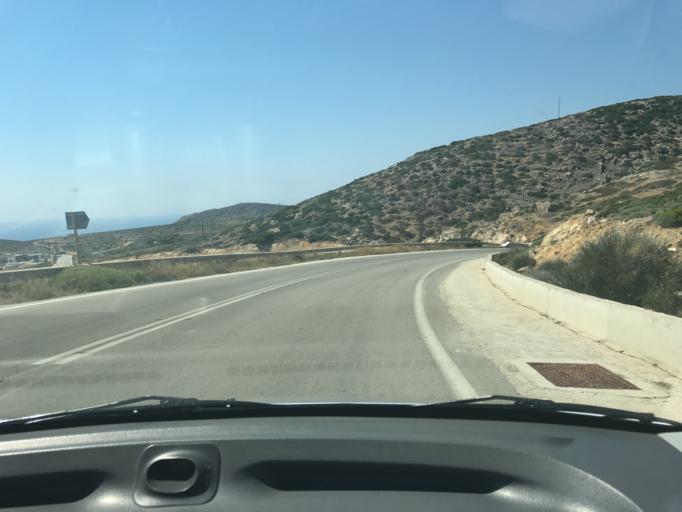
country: GR
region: South Aegean
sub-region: Nomos Dodekanisou
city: Karpathos
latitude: 35.4695
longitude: 27.1368
